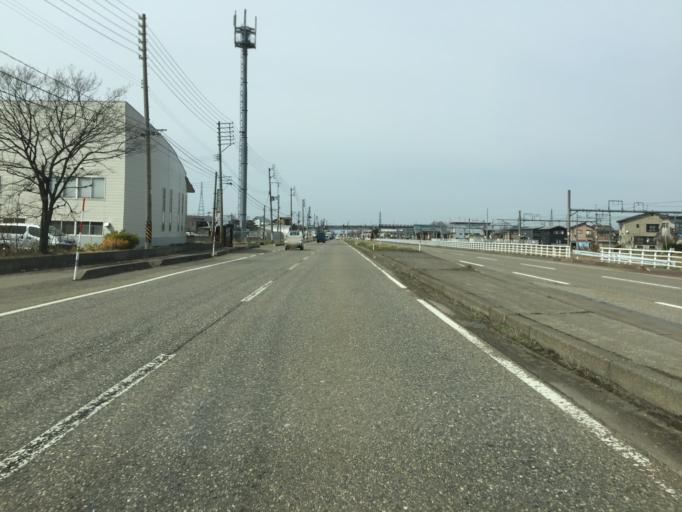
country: JP
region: Niigata
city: Ojiya
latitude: 37.3664
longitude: 138.8345
